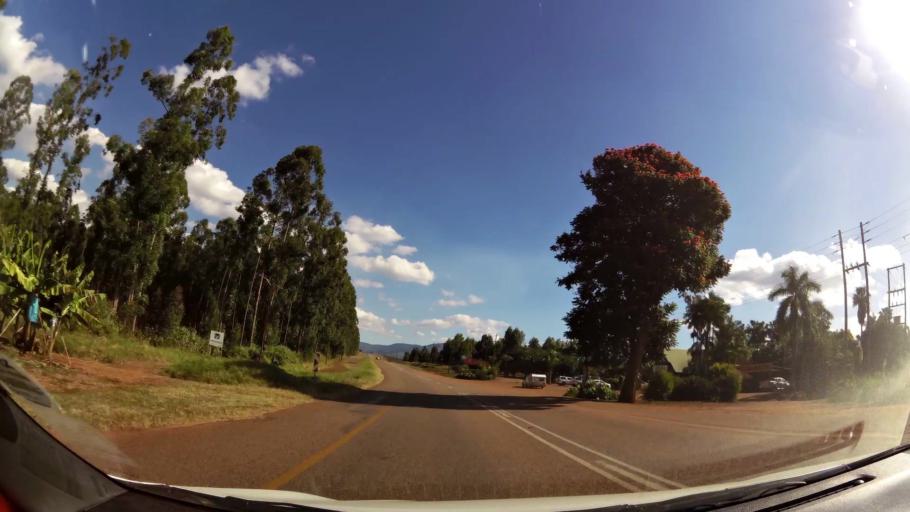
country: ZA
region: Limpopo
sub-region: Mopani District Municipality
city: Tzaneen
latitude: -23.8038
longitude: 30.1066
